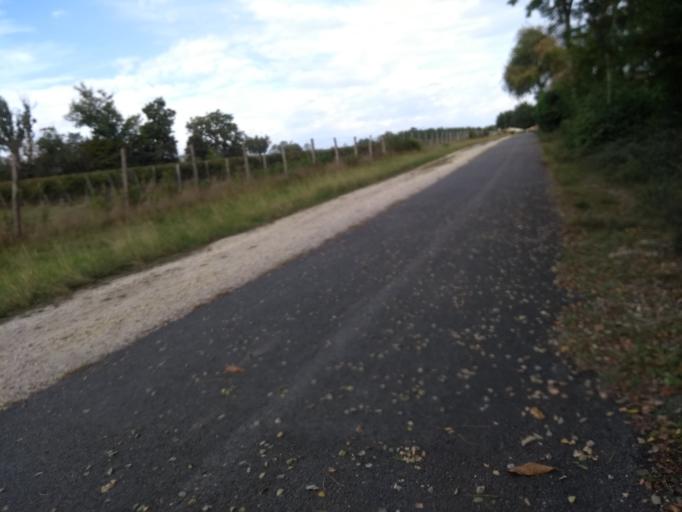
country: FR
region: Aquitaine
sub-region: Departement de la Gironde
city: Canejan
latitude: 44.7615
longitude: -0.6577
